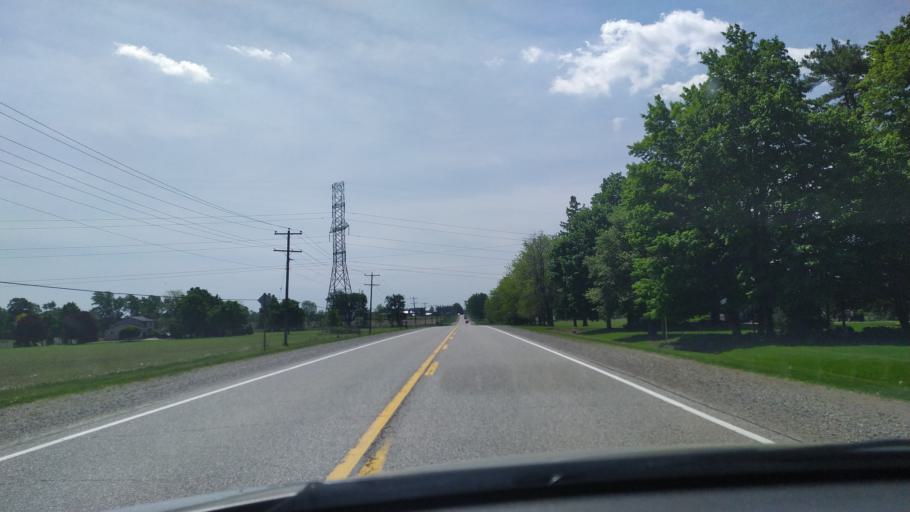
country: CA
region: Ontario
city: Dorchester
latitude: 43.0903
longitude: -81.0053
